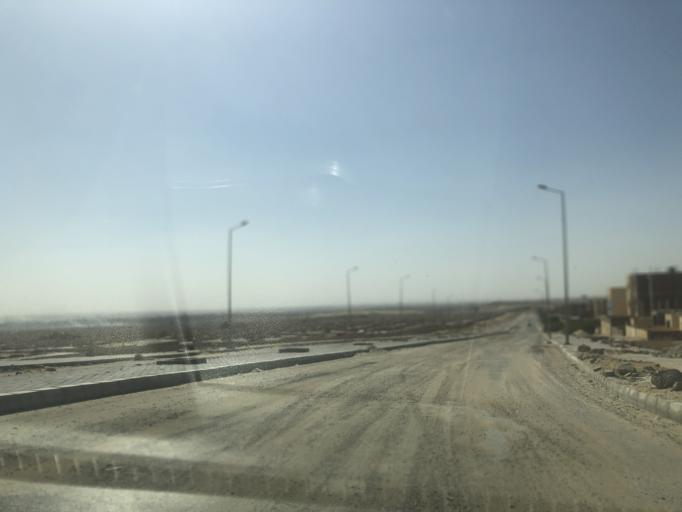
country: EG
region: Al Jizah
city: Madinat Sittah Uktubar
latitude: 29.9297
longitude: 30.9686
